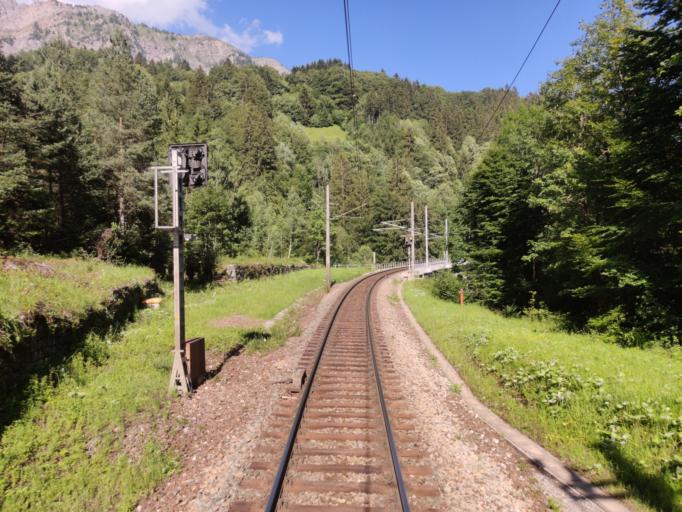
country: AT
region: Vorarlberg
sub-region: Politischer Bezirk Bludenz
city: Dalaas
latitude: 47.1308
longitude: 9.9740
